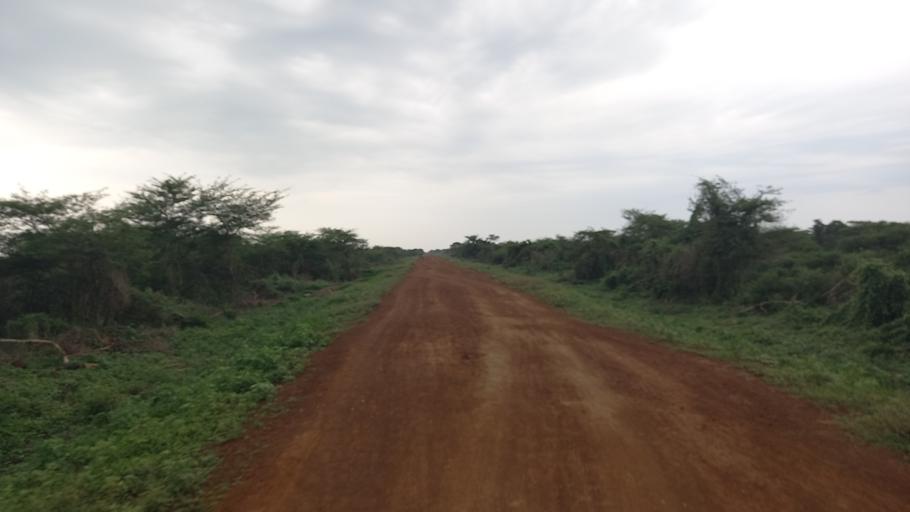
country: ET
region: Gambela
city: Gambela
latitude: 8.3400
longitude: 33.9235
